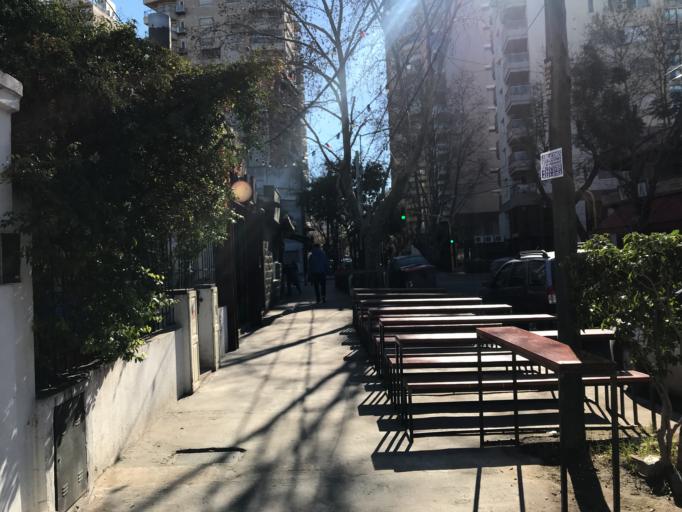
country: AR
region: Buenos Aires
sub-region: Partido de Lomas de Zamora
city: Lomas de Zamora
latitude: -34.7658
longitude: -58.4003
